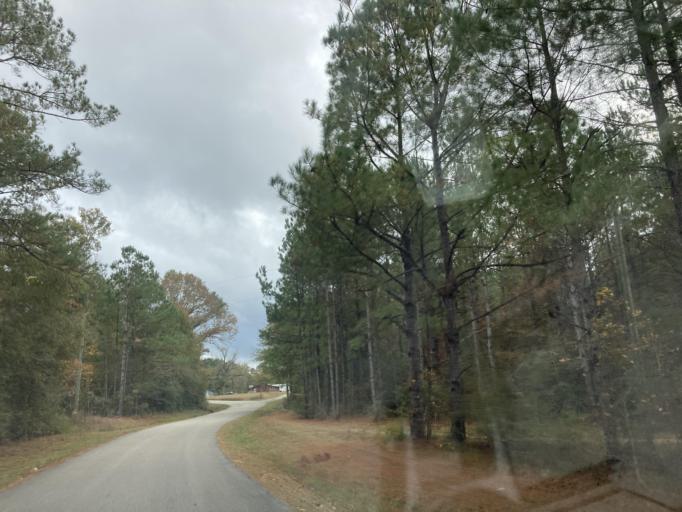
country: US
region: Mississippi
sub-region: Lamar County
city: Purvis
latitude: 31.1511
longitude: -89.5514
